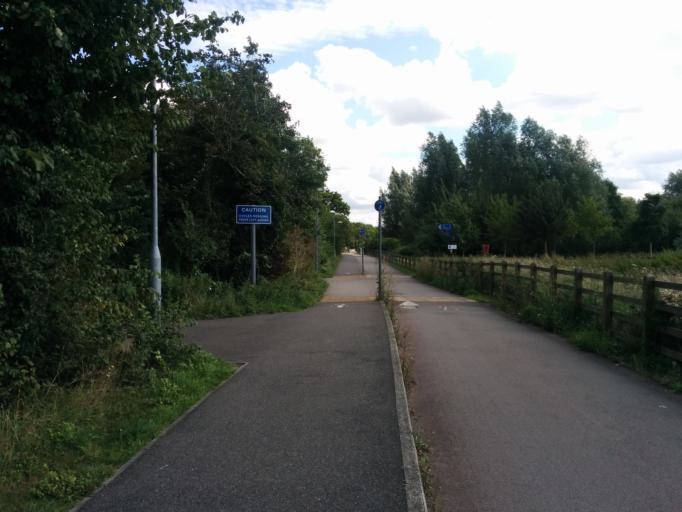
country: GB
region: England
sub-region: Cambridgeshire
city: Cambridge
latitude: 52.2081
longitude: 0.0937
